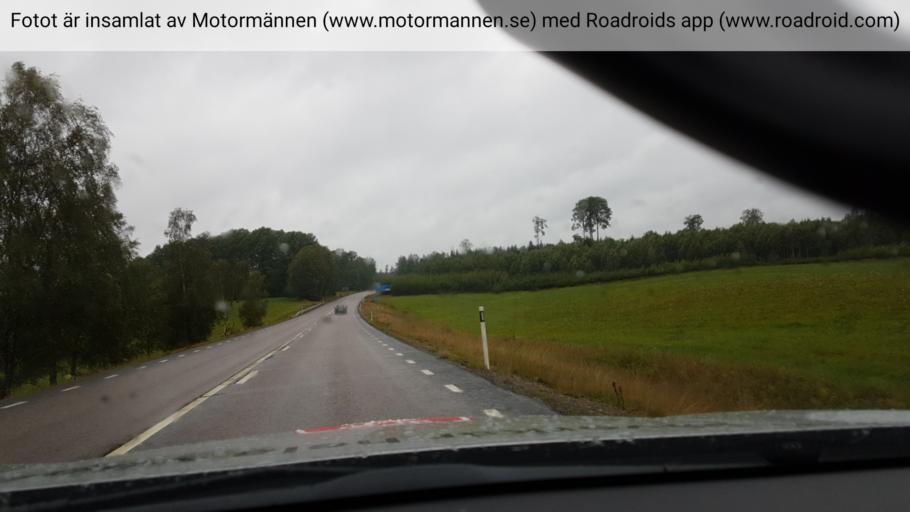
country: SE
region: Vaestra Goetaland
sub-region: Dals-Ed Kommun
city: Ed
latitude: 58.8996
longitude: 11.9684
